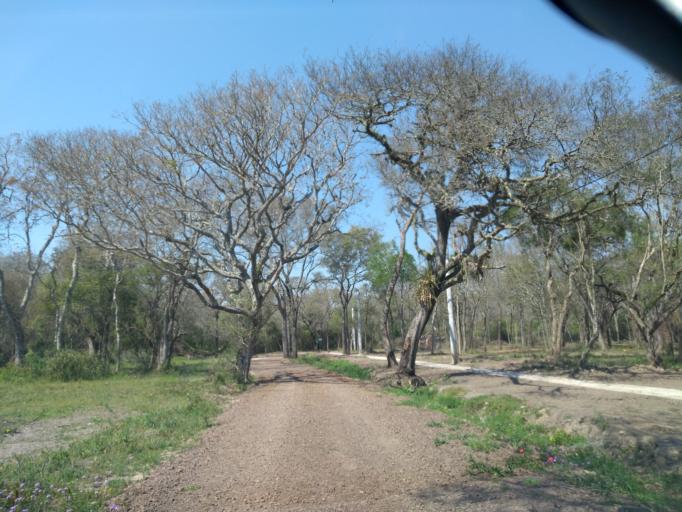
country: AR
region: Chaco
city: Resistencia
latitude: -27.4111
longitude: -58.9546
